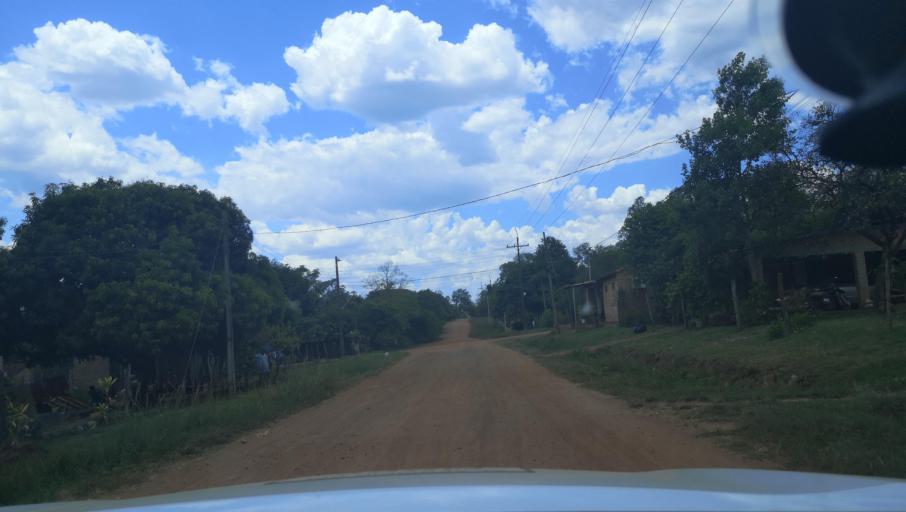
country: PY
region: Itapua
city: Carmen del Parana
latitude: -27.1712
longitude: -56.2444
